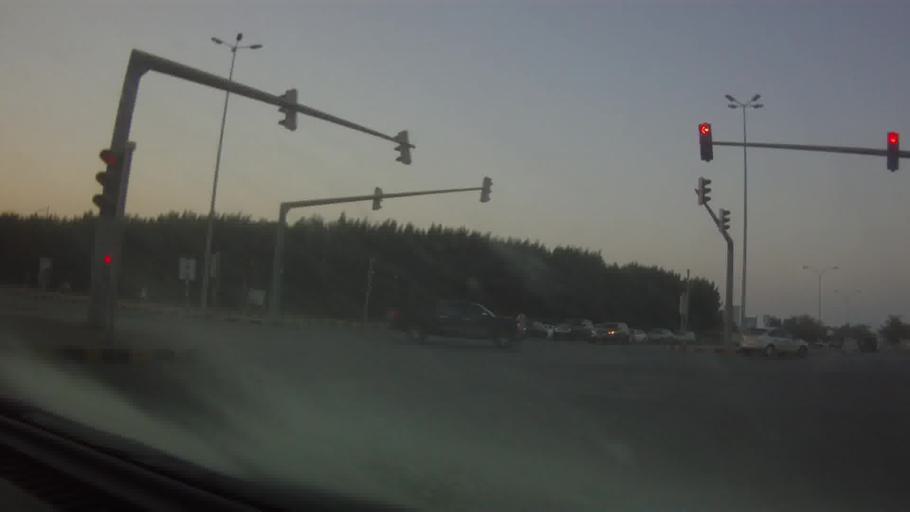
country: OM
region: Muhafazat Masqat
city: Bawshar
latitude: 23.6004
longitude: 58.4414
